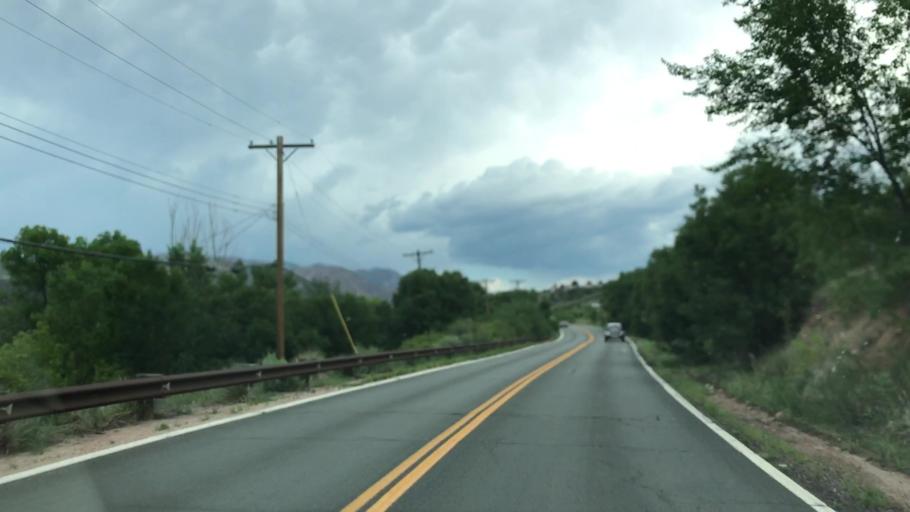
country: US
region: Colorado
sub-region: El Paso County
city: Manitou Springs
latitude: 38.8701
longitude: -104.8680
